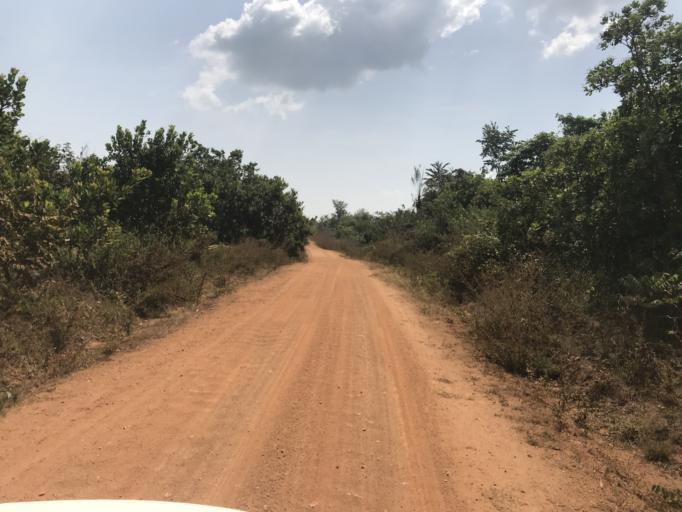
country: NG
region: Osun
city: Ifon
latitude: 7.9891
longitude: 4.5161
